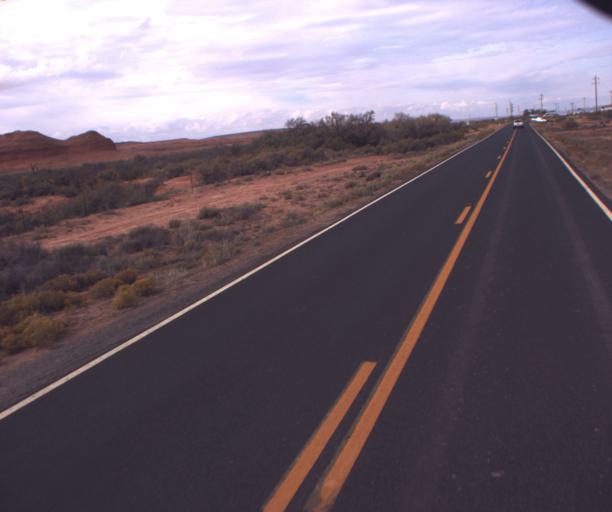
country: US
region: Arizona
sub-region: Apache County
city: Many Farms
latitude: 36.7118
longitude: -109.6241
